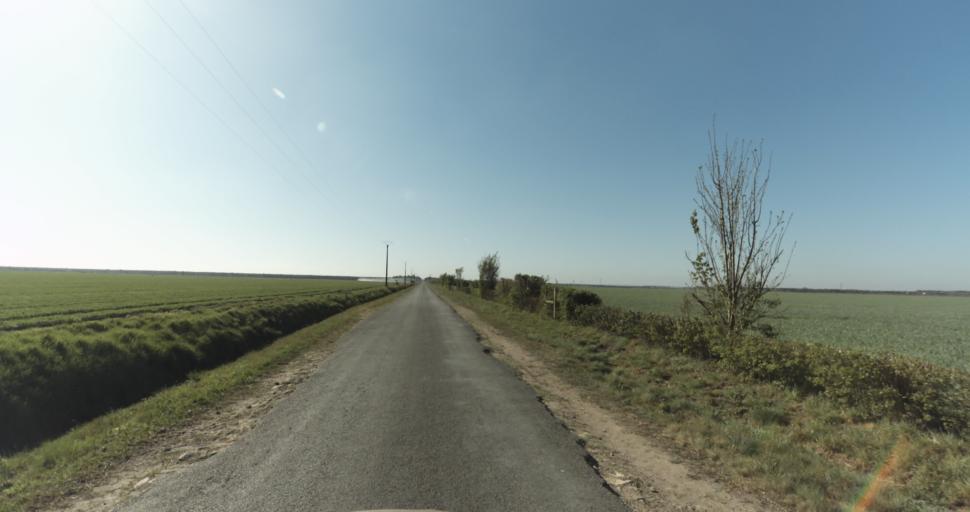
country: FR
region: Aquitaine
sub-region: Departement de la Gironde
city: Marcheprime
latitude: 44.7736
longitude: -0.8580
